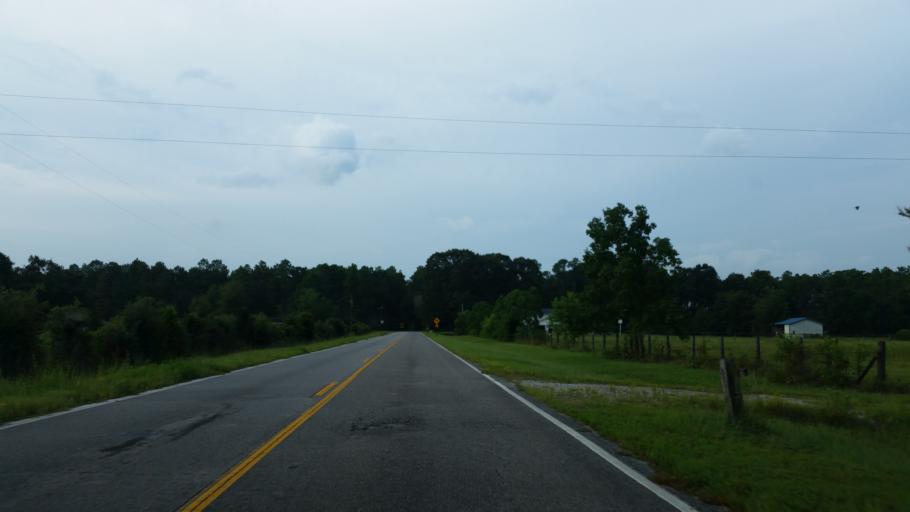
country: US
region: Florida
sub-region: Escambia County
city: Molino
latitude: 30.7733
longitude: -87.5234
